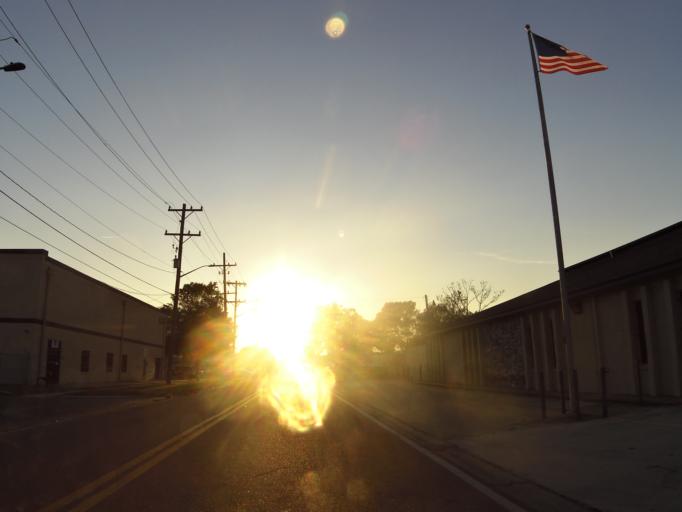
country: US
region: Florida
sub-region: Duval County
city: Jacksonville
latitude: 30.3193
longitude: -81.6943
